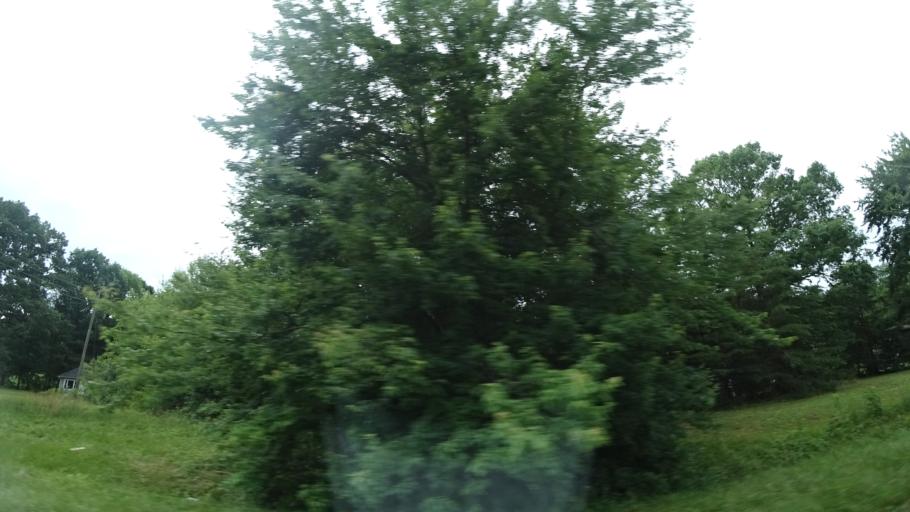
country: US
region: Virginia
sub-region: Spotsylvania County
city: Spotsylvania
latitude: 38.1390
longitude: -77.7242
